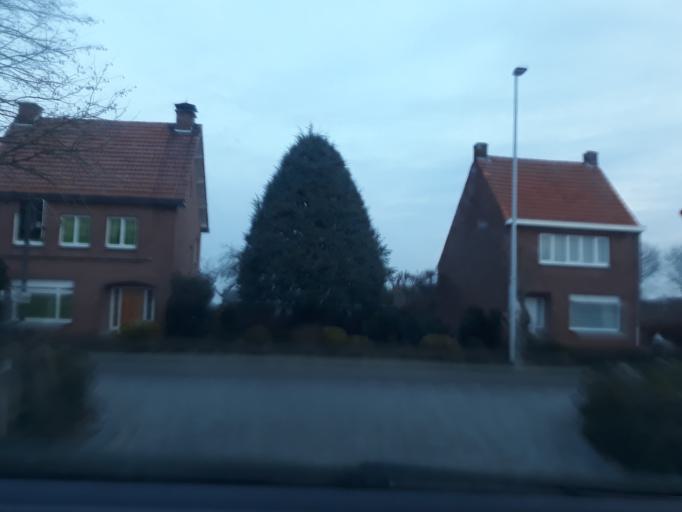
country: BE
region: Flanders
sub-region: Provincie Antwerpen
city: Ravels
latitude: 51.4097
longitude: 4.9968
